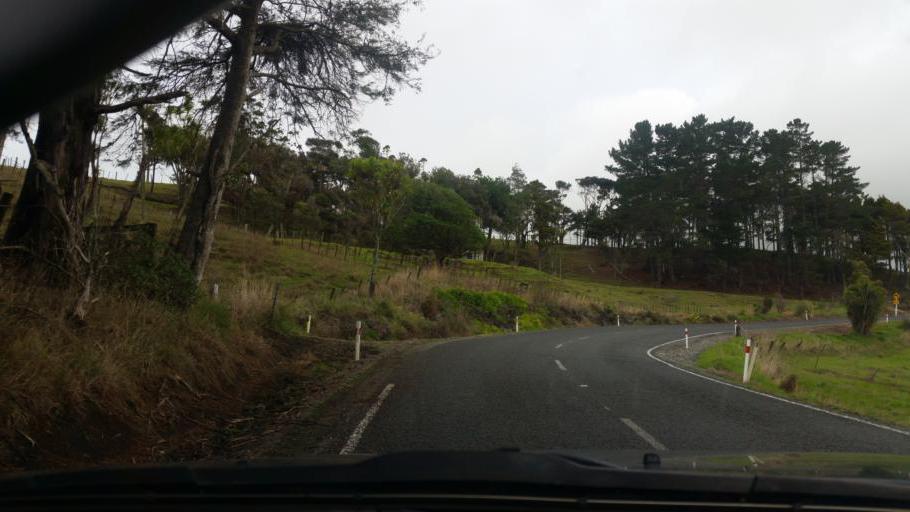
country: NZ
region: Northland
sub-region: Kaipara District
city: Dargaville
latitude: -36.0132
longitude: 173.9795
